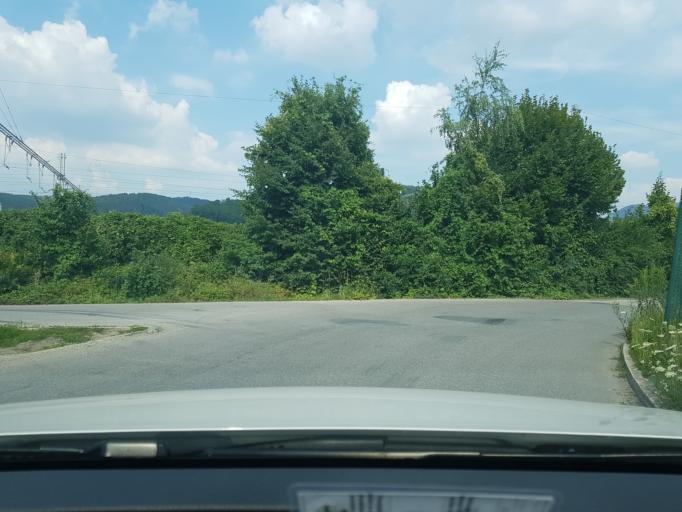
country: SK
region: Trenciansky
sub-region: Okres Povazska Bystrica
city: Povazska Bystrica
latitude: 49.1252
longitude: 18.4234
